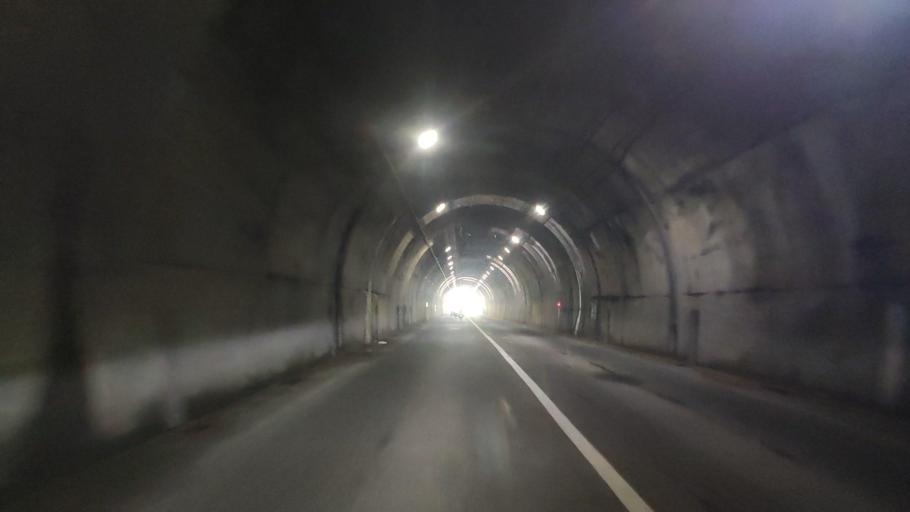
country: JP
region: Fukui
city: Tsuruga
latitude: 35.6696
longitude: 136.0850
